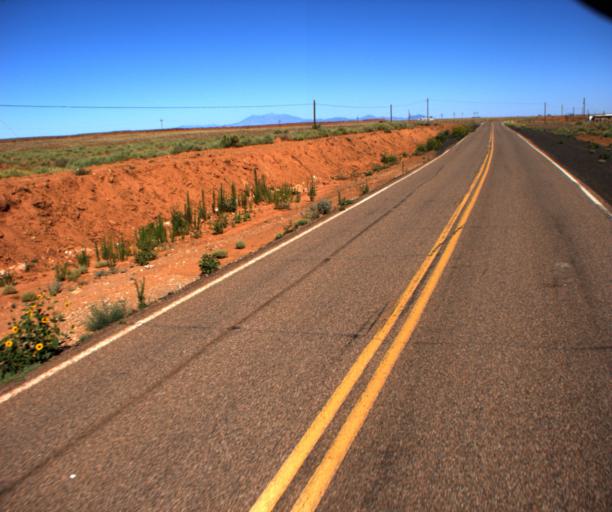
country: US
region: Arizona
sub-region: Coconino County
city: LeChee
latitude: 35.1533
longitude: -110.9006
